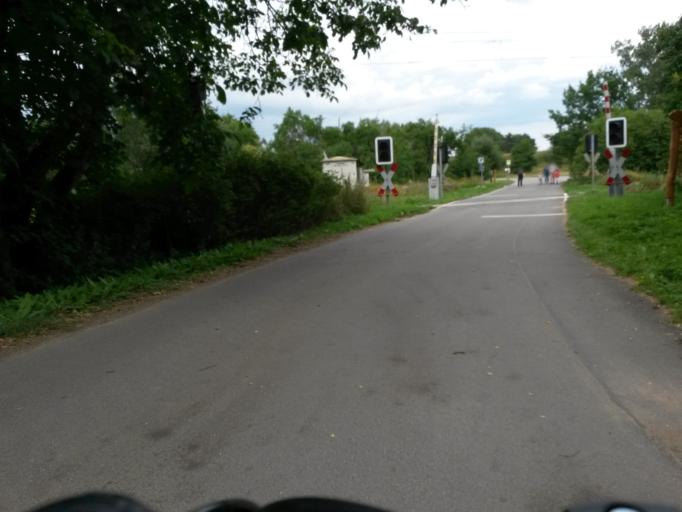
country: DE
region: Brandenburg
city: Angermunde
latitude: 53.0357
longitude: 13.9664
